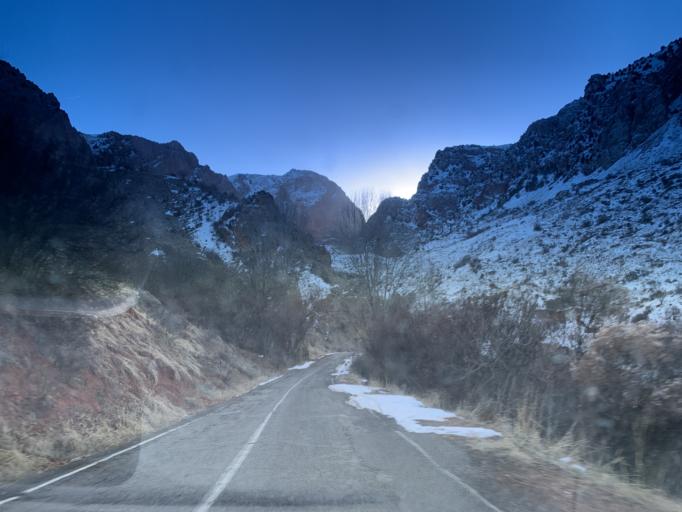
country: AM
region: Vayots' Dzori Marz
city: Areni
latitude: 39.6833
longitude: 45.2333
